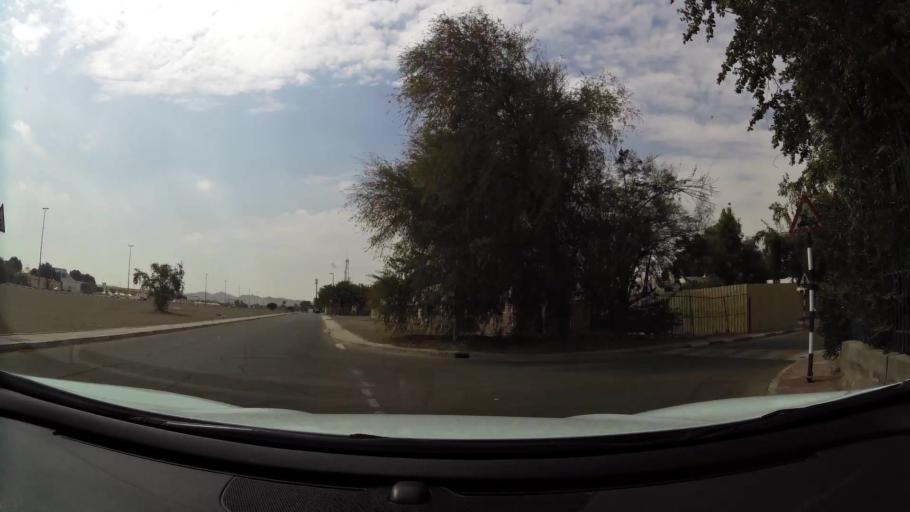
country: AE
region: Abu Dhabi
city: Al Ain
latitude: 24.1962
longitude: 55.7947
